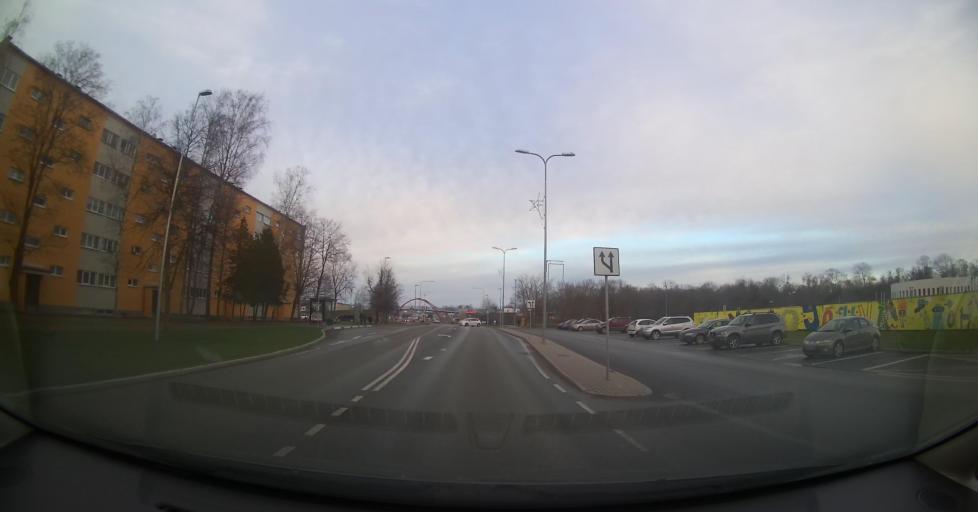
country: EE
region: Ida-Virumaa
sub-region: Johvi vald
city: Johvi
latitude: 59.3478
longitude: 27.4194
